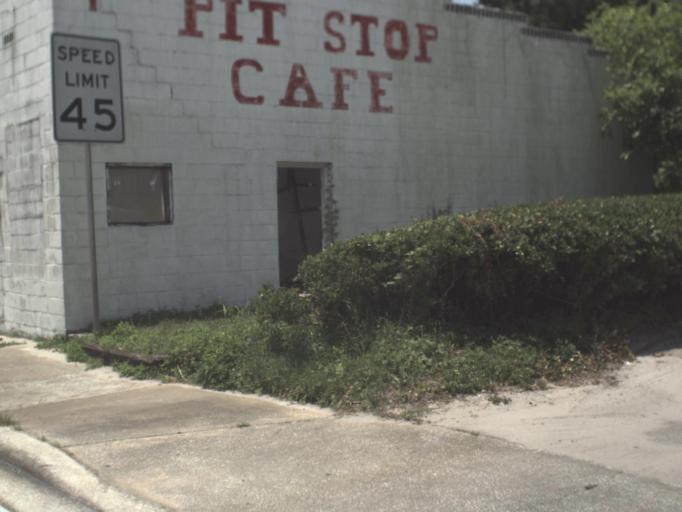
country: US
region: Florida
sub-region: Bradford County
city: Starke
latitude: 30.0437
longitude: -82.0722
